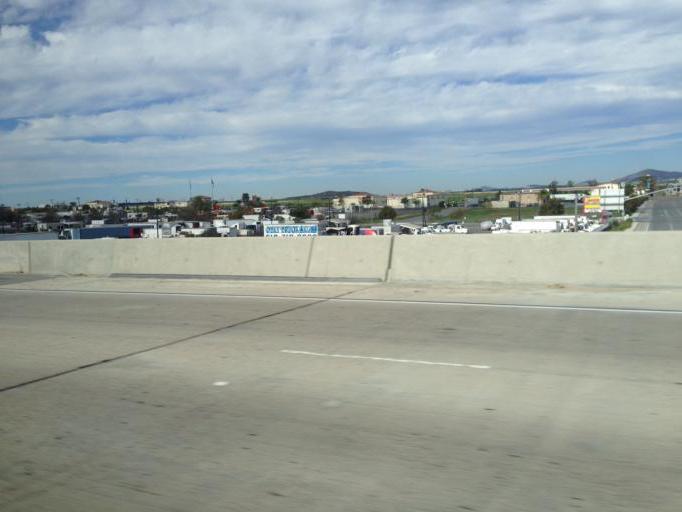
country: MX
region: Baja California
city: Tijuana
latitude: 32.5643
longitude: -116.9623
